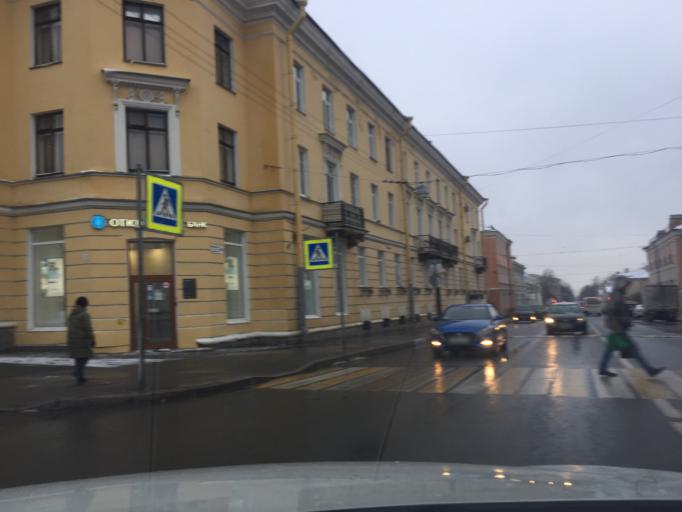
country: RU
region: St.-Petersburg
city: Pushkin
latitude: 59.7176
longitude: 30.4061
